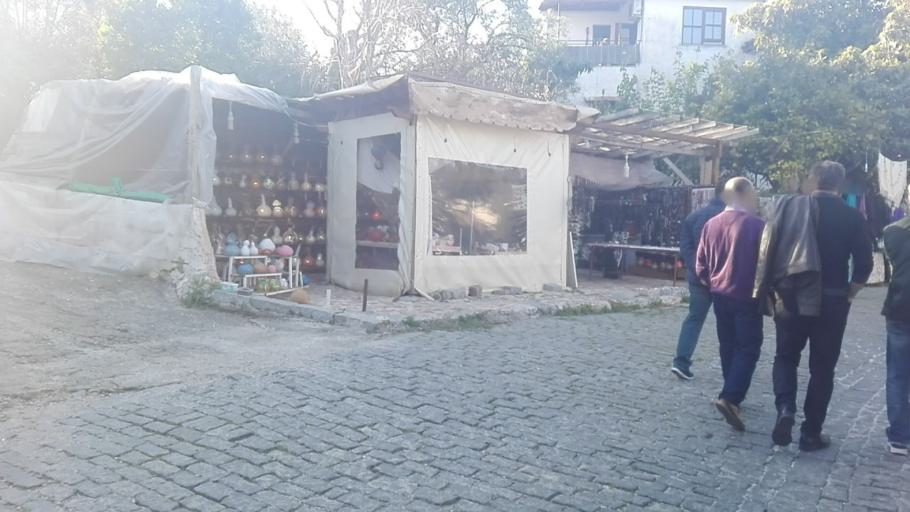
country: TR
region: Antalya
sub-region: Alanya
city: Alanya
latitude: 36.5333
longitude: 31.9932
